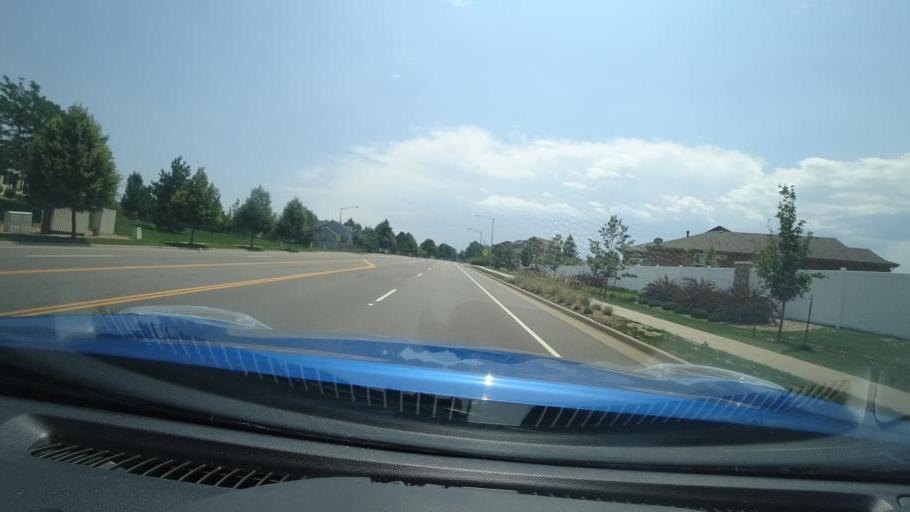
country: US
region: Colorado
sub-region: Adams County
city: Aurora
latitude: 39.6795
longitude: -104.7625
